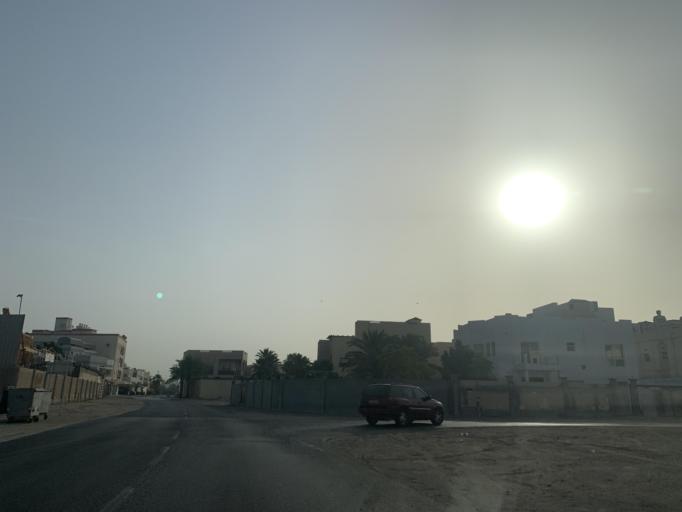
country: BH
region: Northern
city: Madinat `Isa
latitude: 26.1934
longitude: 50.5577
